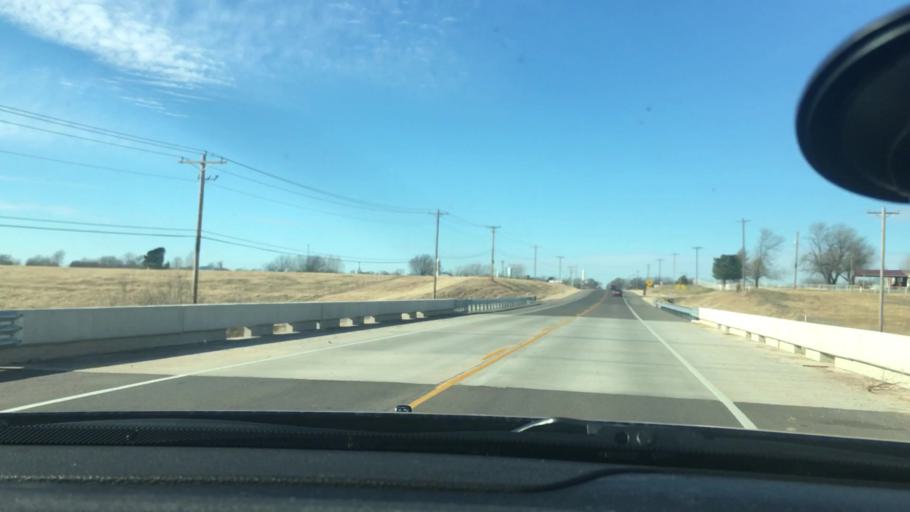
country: US
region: Oklahoma
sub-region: Cleveland County
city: Lexington
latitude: 35.0149
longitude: -97.3135
